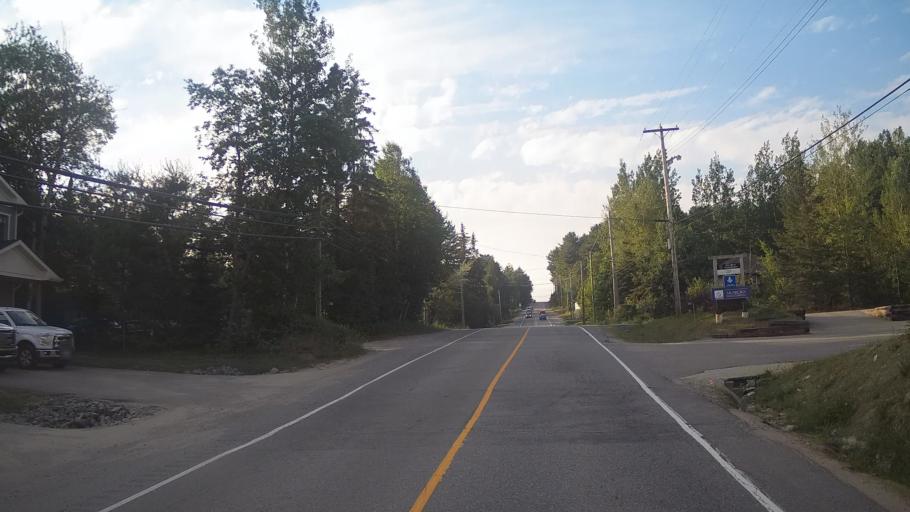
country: CA
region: Ontario
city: Huntsville
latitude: 45.3519
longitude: -79.2017
